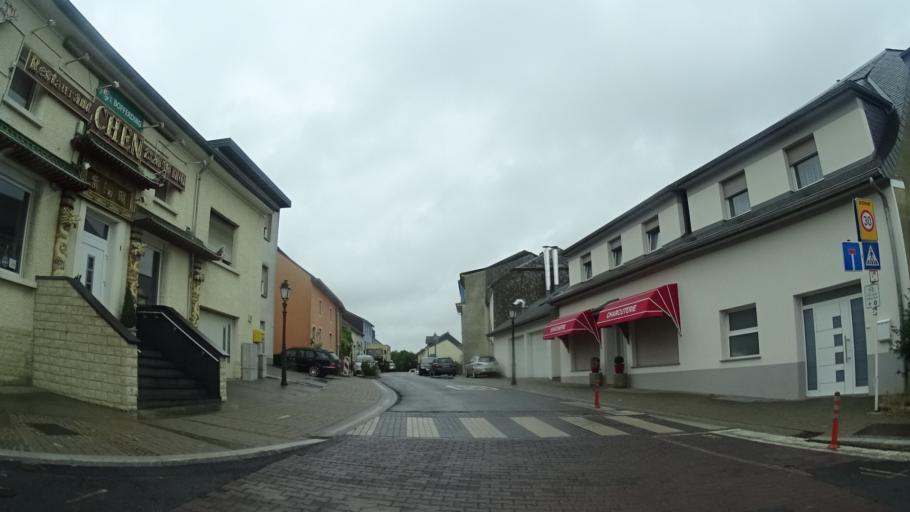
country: LU
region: Luxembourg
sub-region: Canton d'Esch-sur-Alzette
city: Sanem
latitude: 49.5486
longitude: 5.9296
